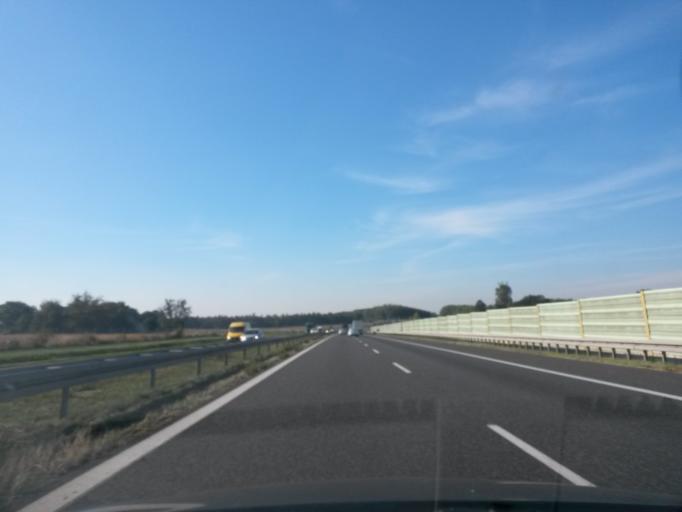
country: PL
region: Silesian Voivodeship
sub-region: Powiat gliwicki
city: Rudziniec
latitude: 50.3787
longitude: 18.4710
